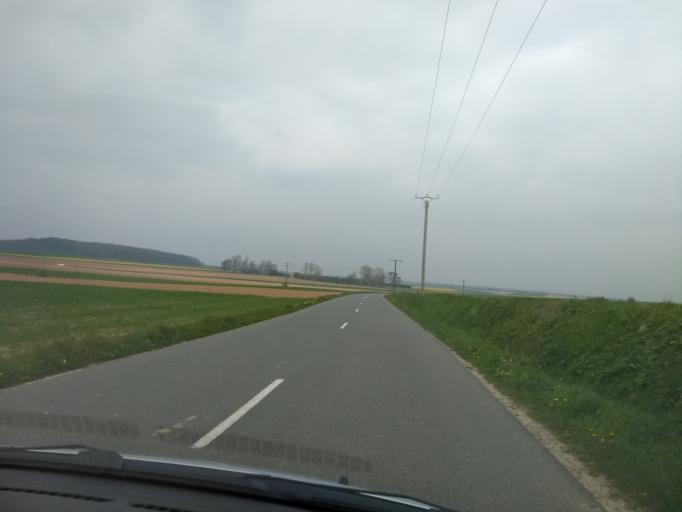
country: FR
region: Nord-Pas-de-Calais
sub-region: Departement du Pas-de-Calais
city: Mont-Saint-Eloi
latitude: 50.3497
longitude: 2.7108
